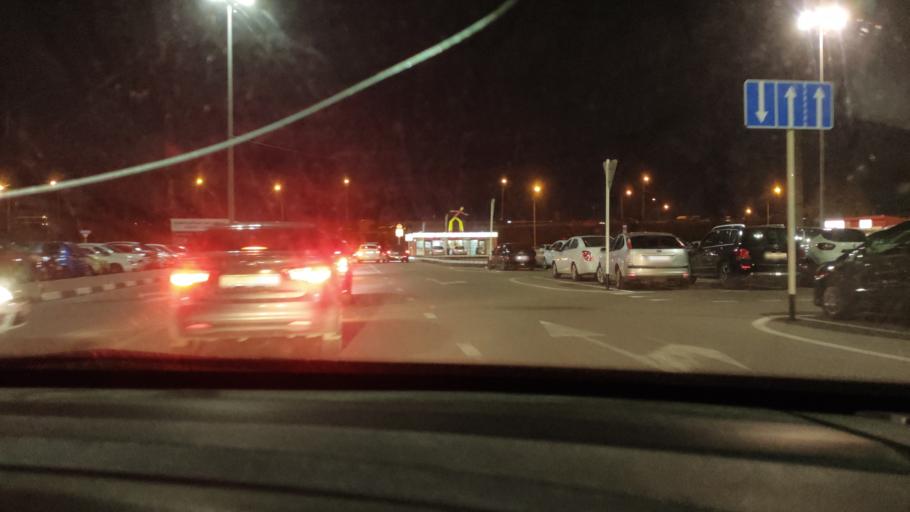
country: RU
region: Krasnodarskiy
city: Krasnodar
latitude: 45.1018
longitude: 38.9887
